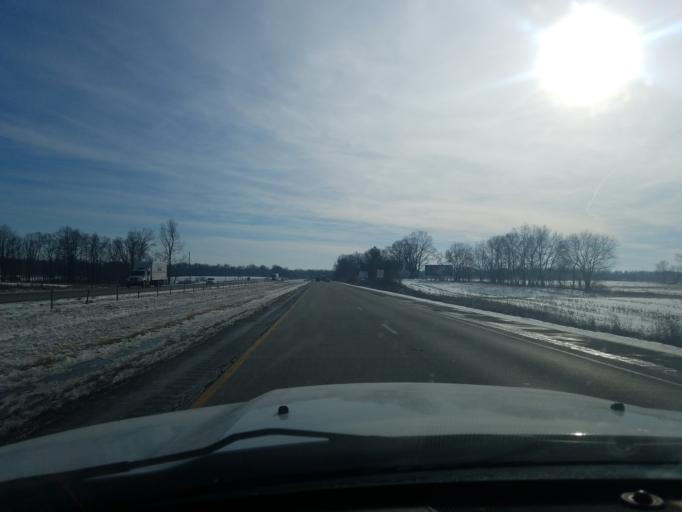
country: US
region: Indiana
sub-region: Grant County
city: Upland
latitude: 40.4683
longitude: -85.5501
